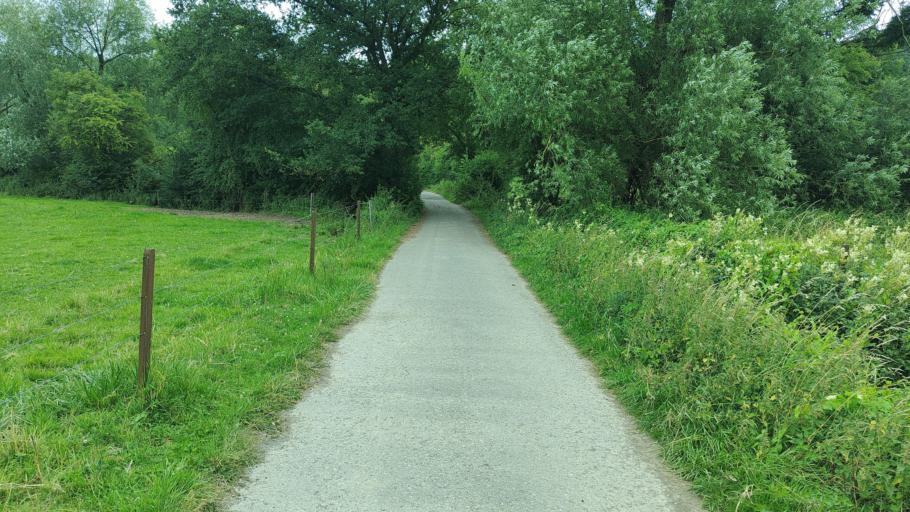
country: BE
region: Wallonia
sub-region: Province du Hainaut
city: Chimay
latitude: 50.0534
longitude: 4.3942
